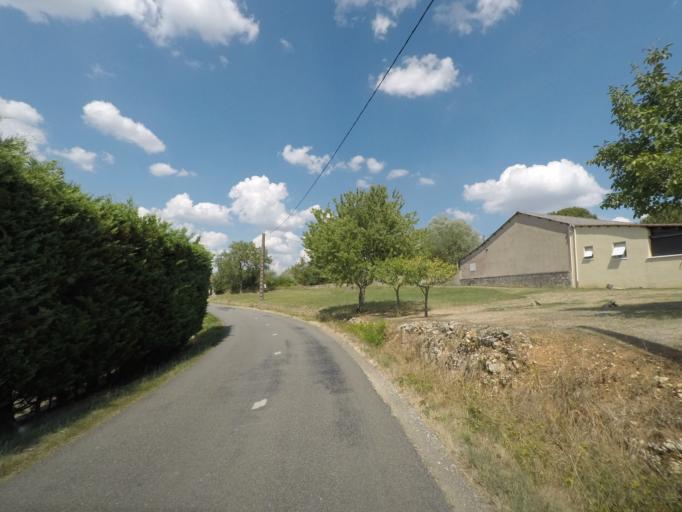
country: FR
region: Midi-Pyrenees
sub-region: Departement du Lot
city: Cahors
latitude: 44.5902
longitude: 1.5811
